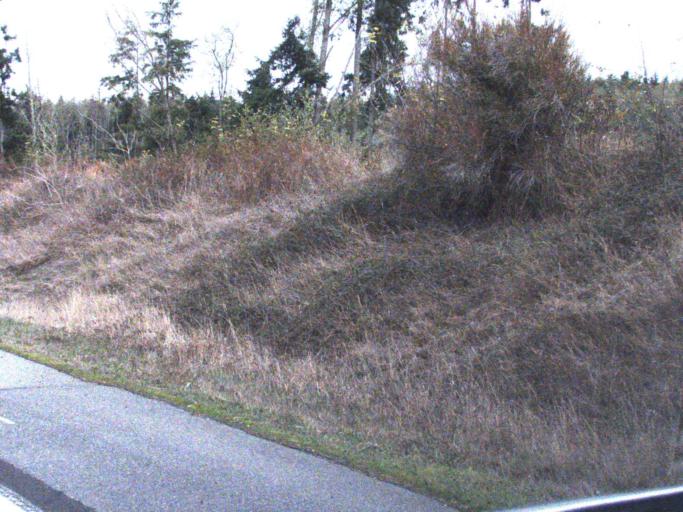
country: US
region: Washington
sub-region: Island County
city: Camano
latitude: 48.1495
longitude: -122.5942
